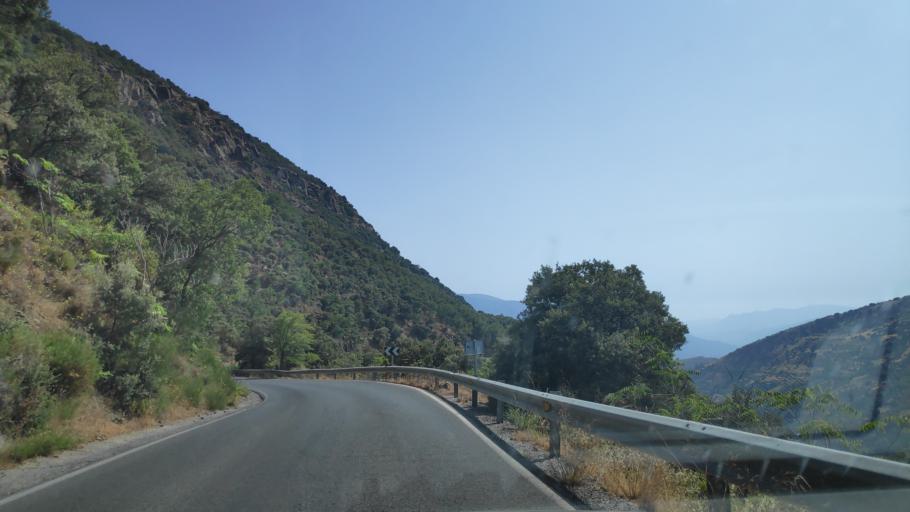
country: ES
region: Andalusia
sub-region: Provincia de Granada
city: Pampaneira
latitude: 36.9397
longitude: -3.3569
